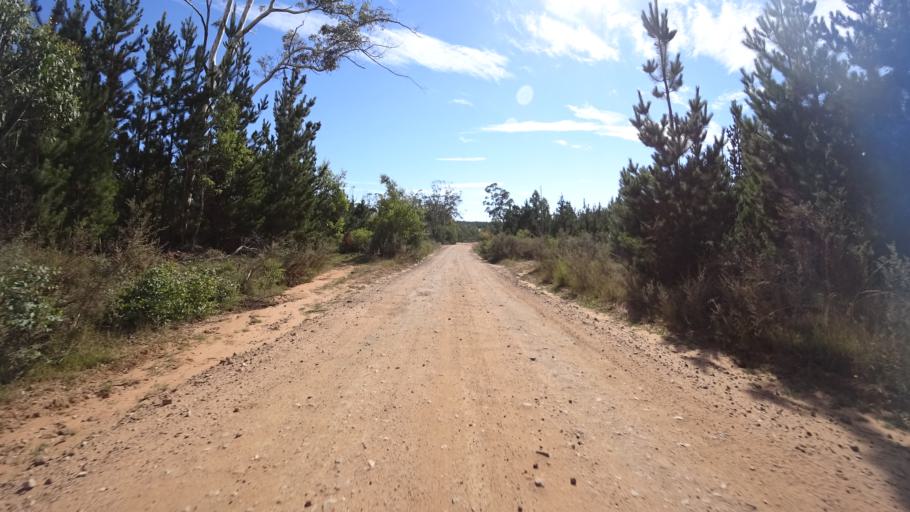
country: AU
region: New South Wales
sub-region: Lithgow
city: Lithgow
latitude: -33.3584
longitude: 150.2513
